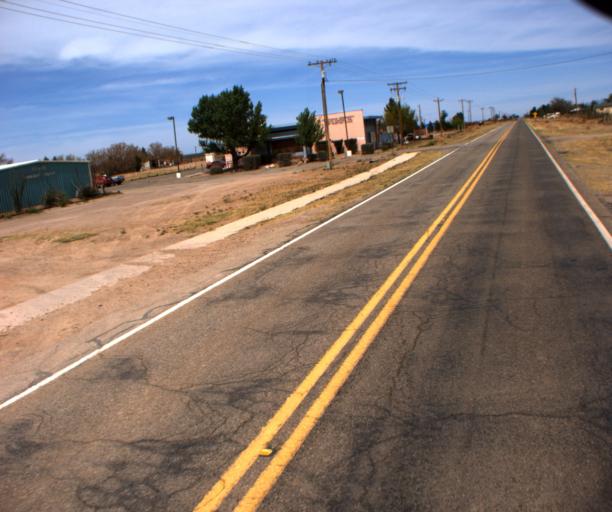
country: US
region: Arizona
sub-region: Cochise County
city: Bisbee
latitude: 31.6963
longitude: -109.6872
